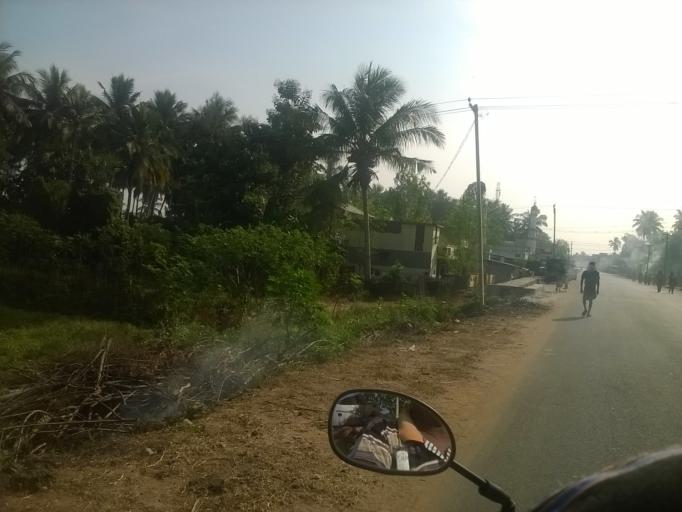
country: IN
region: Tamil Nadu
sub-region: Thanjavur
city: Thiruvaiyaru
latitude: 10.8986
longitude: 79.0500
